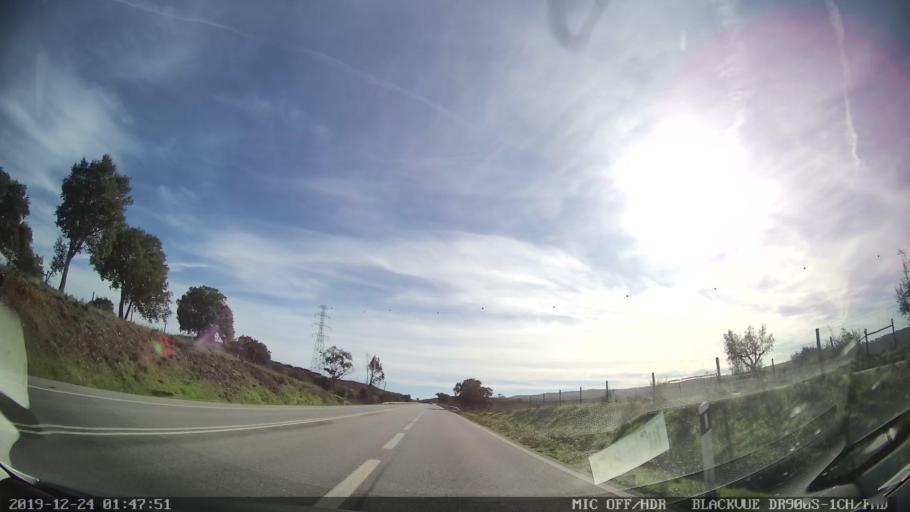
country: PT
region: Portalegre
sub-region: Nisa
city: Nisa
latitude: 39.5270
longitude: -7.7854
